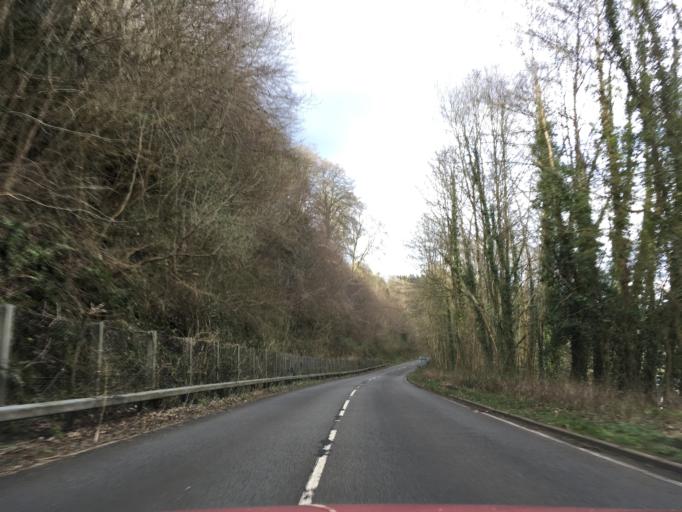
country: GB
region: Wales
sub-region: Monmouthshire
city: Tintern
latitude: 51.7130
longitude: -2.6788
